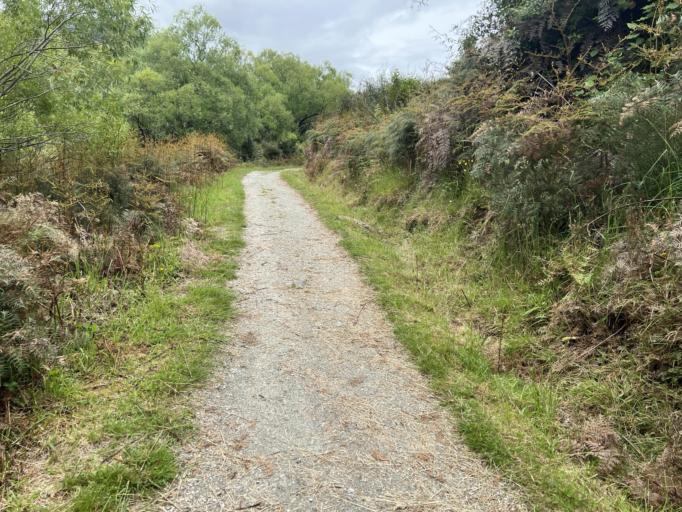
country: NZ
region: Otago
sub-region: Queenstown-Lakes District
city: Wanaka
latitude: -44.6477
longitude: 168.9624
